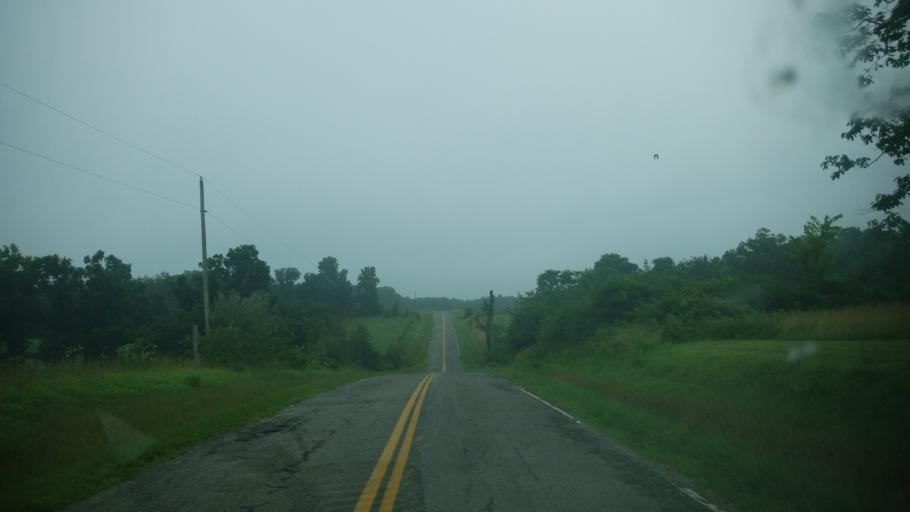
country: US
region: Missouri
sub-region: Audrain County
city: Vandalia
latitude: 39.2817
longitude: -91.3462
